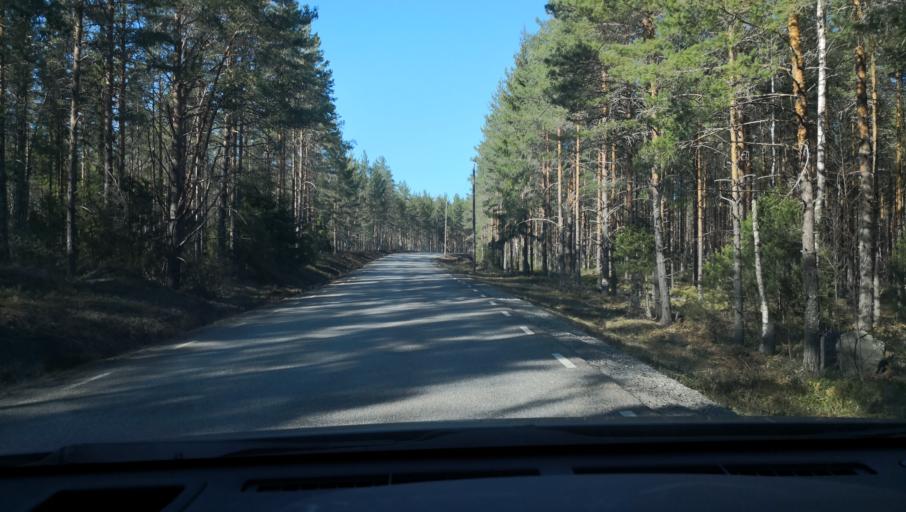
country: SE
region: Vaestmanland
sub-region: Sala Kommun
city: Sala
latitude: 60.0025
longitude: 16.4950
